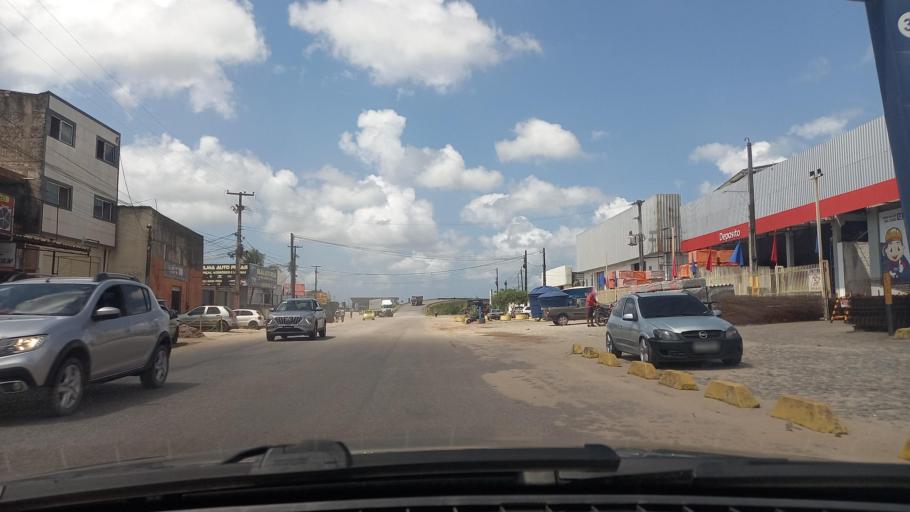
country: BR
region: Pernambuco
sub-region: Goiana
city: Goiana
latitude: -7.5663
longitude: -34.9937
